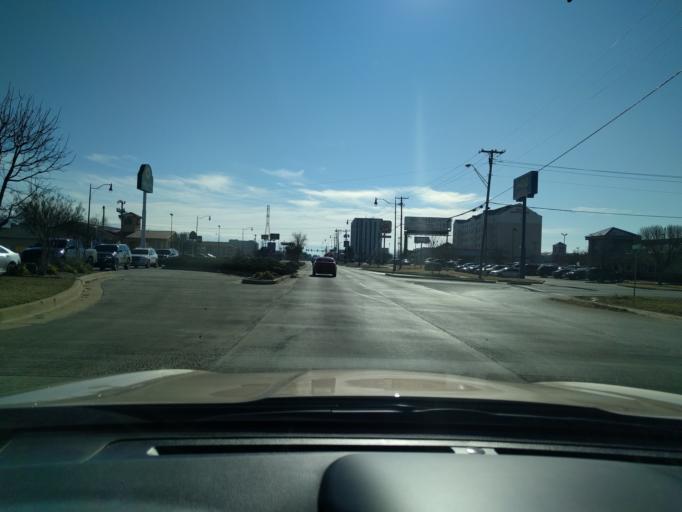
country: US
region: Oklahoma
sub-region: Oklahoma County
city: Warr Acres
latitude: 35.4597
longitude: -97.6012
